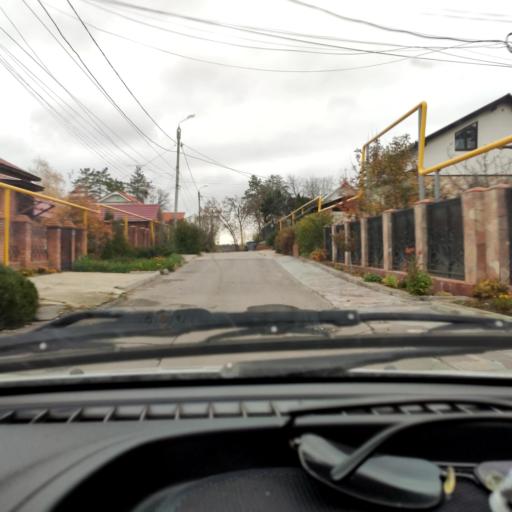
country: RU
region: Samara
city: Tol'yatti
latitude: 53.4799
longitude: 49.3576
